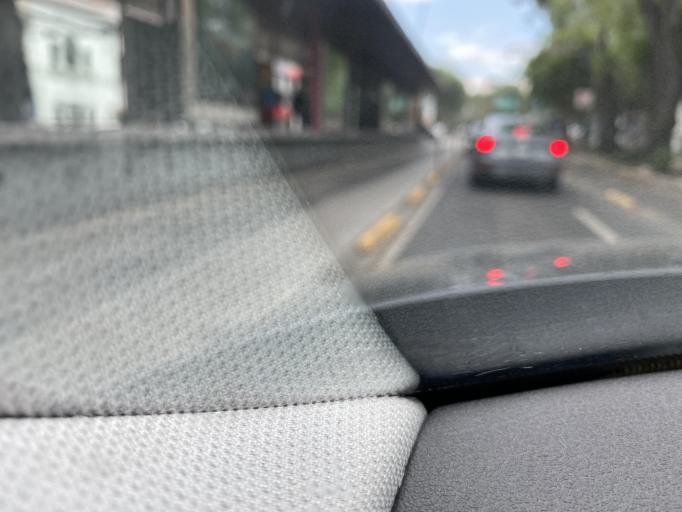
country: MX
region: Mexico City
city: Benito Juarez
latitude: 19.3952
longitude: -99.1469
